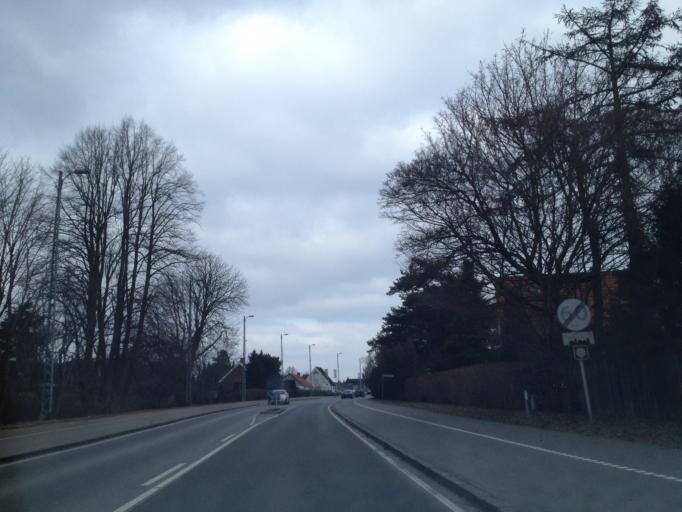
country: DK
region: Capital Region
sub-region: Fredensborg Kommune
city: Humlebaek
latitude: 55.9792
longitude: 12.5447
